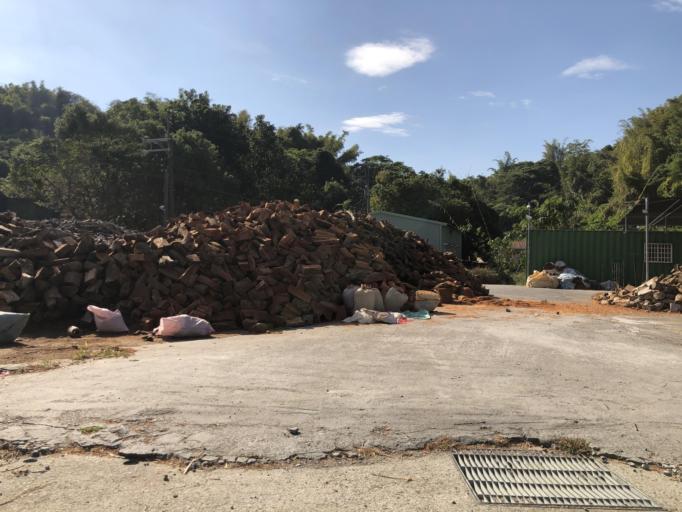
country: TW
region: Taiwan
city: Yujing
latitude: 23.0134
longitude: 120.3855
